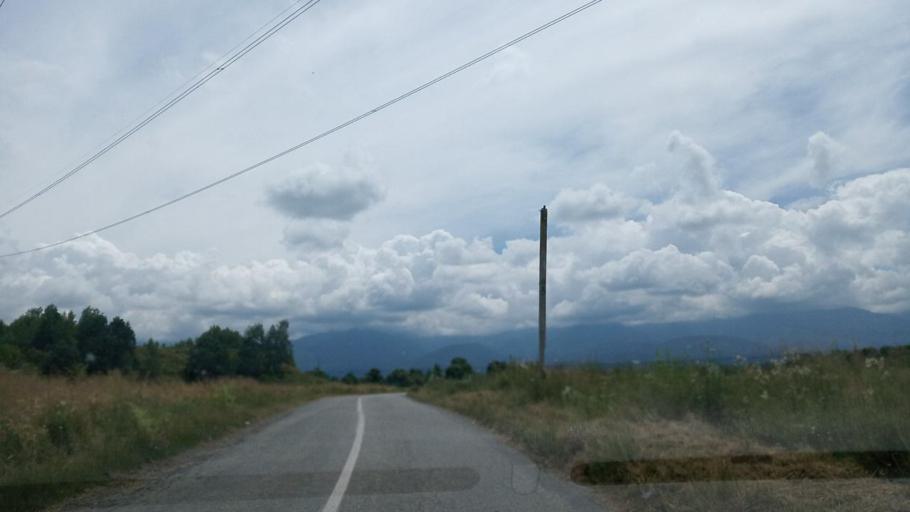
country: RO
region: Sibiu
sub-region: Comuna Porumbacu de Jos
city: Porumbacu de Jos
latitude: 45.7270
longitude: 24.4713
